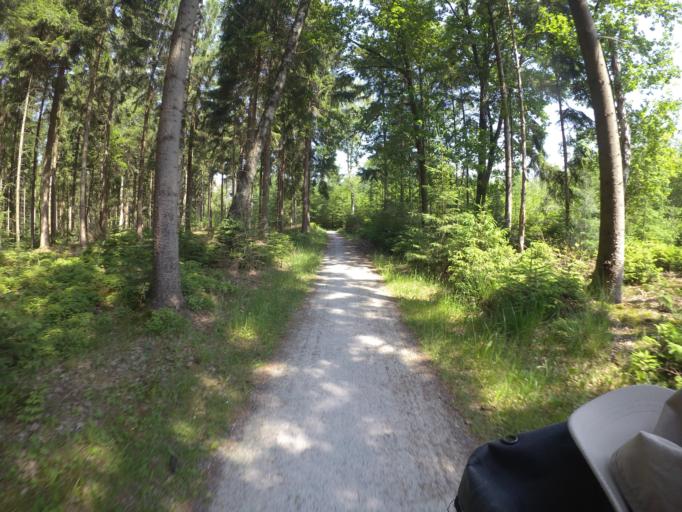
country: NL
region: Drenthe
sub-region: Gemeente De Wolden
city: Ruinen
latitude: 52.7258
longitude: 6.3642
